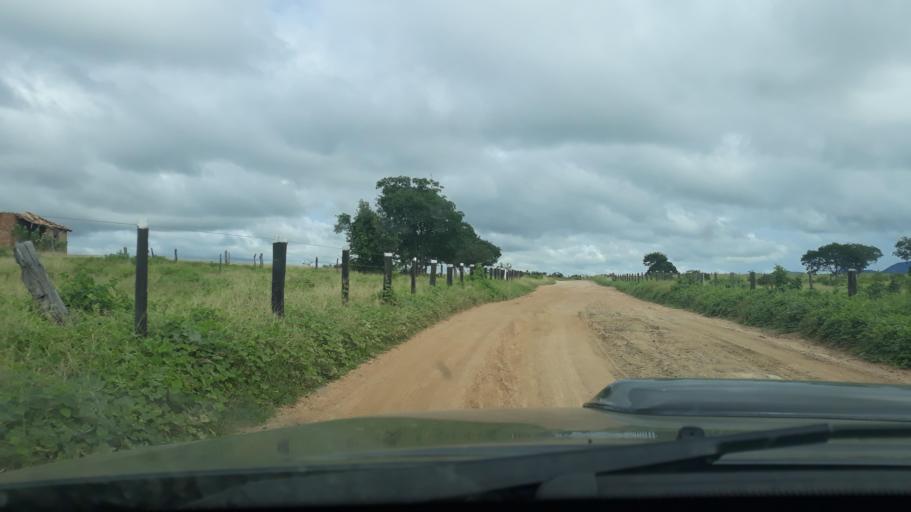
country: BR
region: Bahia
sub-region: Riacho De Santana
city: Riacho de Santana
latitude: -13.9017
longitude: -42.8651
